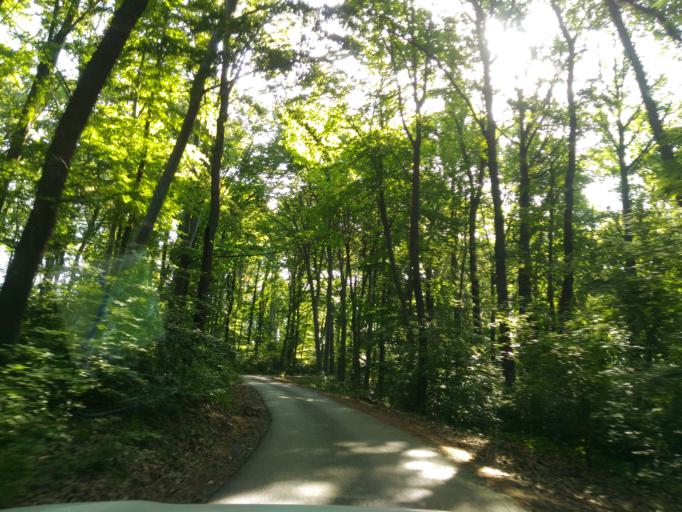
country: HU
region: Baranya
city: Hosszuheteny
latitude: 46.2145
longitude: 18.3539
